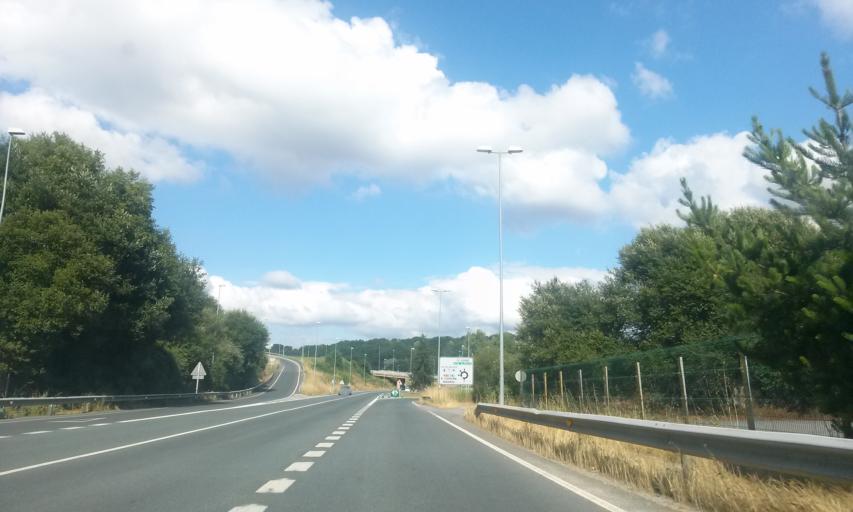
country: ES
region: Galicia
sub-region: Provincia de Lugo
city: Lugo
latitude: 42.9898
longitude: -7.5435
